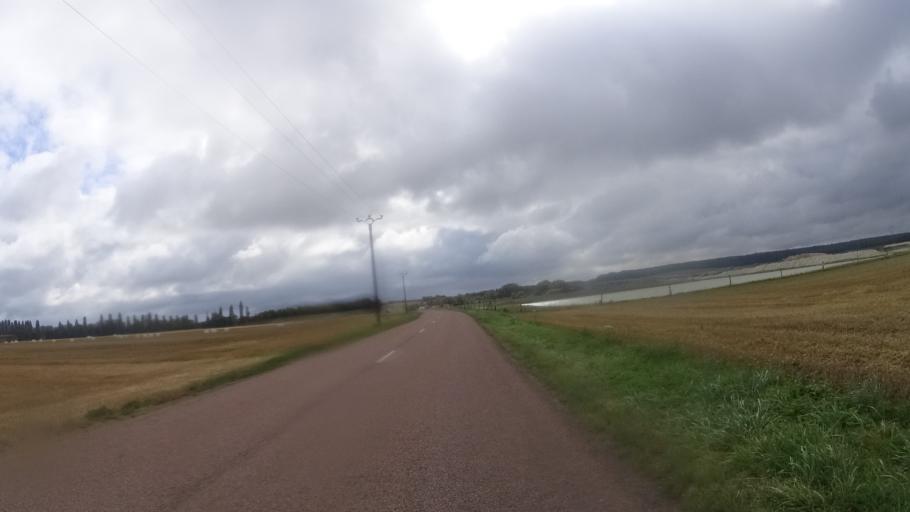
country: FR
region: Champagne-Ardenne
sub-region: Departement de l'Aube
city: Brienne-le-Chateau
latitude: 48.3482
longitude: 4.5699
